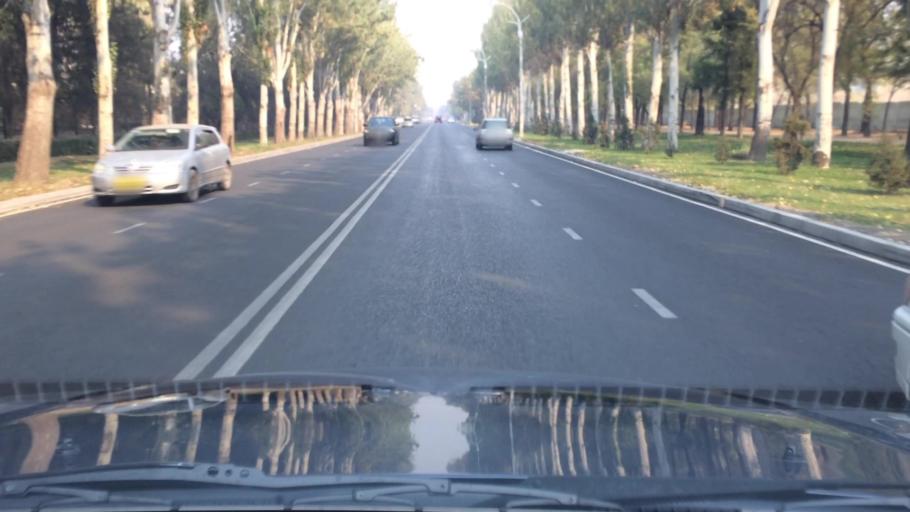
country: KG
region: Chuy
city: Bishkek
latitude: 42.8379
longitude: 74.5858
